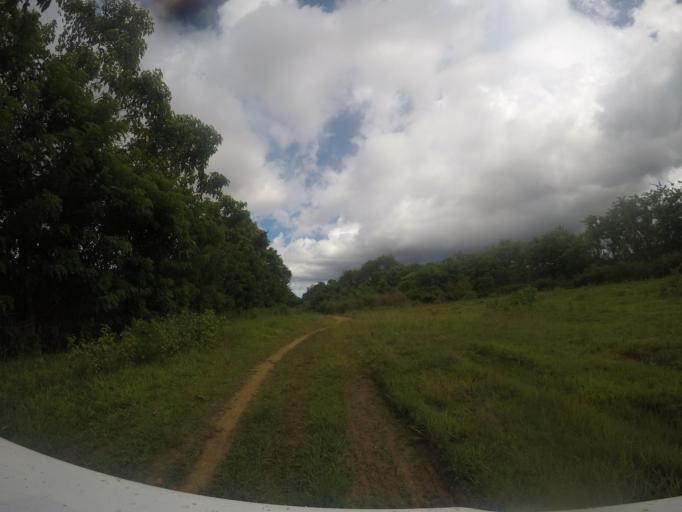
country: TL
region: Lautem
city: Lospalos
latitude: -8.5068
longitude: 127.0107
